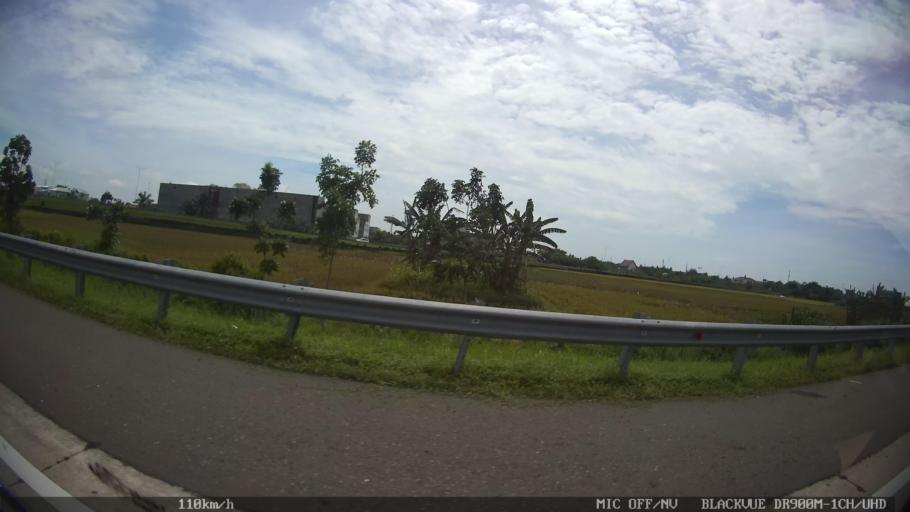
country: ID
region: North Sumatra
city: Percut
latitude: 3.5567
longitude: 98.8522
